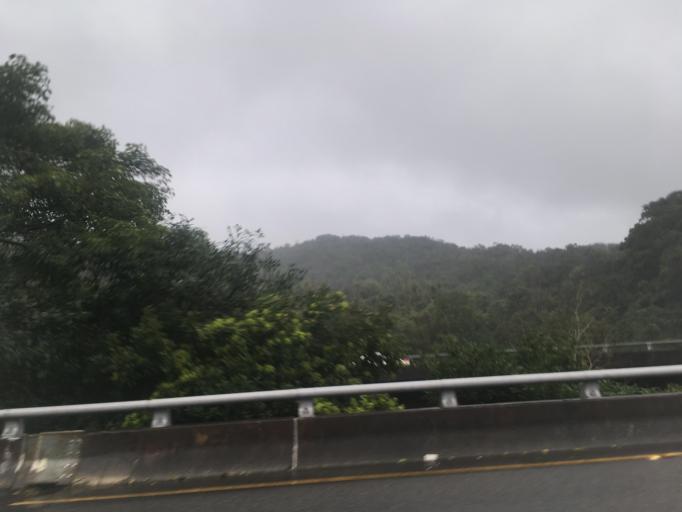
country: TW
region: Taiwan
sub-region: Keelung
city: Keelung
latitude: 25.0927
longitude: 121.6626
